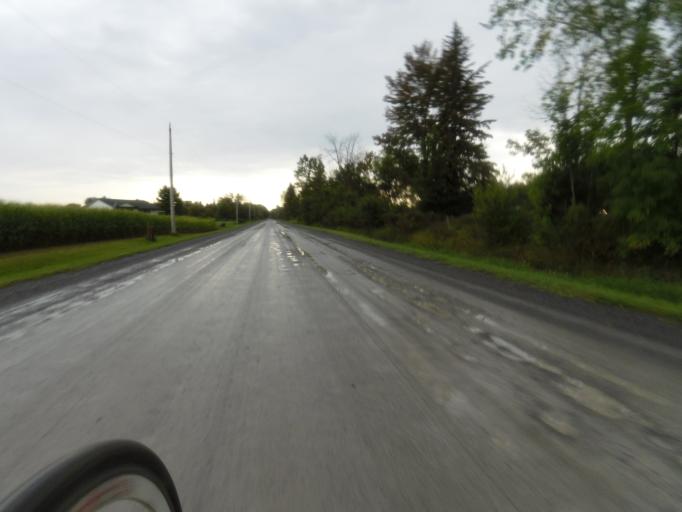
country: CA
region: Ontario
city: Bells Corners
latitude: 45.1739
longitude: -75.7012
